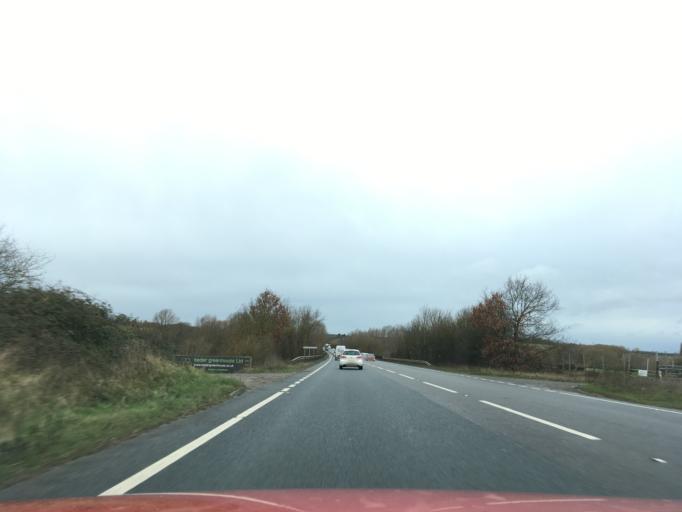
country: GB
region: England
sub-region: Worcestershire
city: Evesham
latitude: 52.1046
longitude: -1.9275
